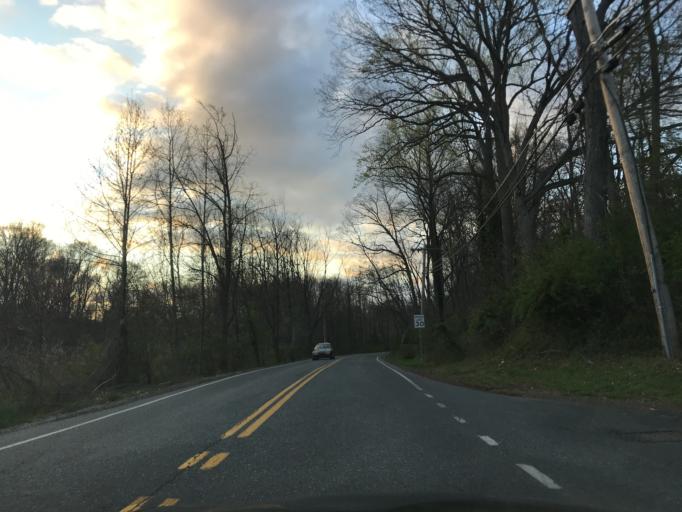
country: US
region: Maryland
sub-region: Harford County
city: Bel Air South
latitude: 39.5264
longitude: -76.3158
